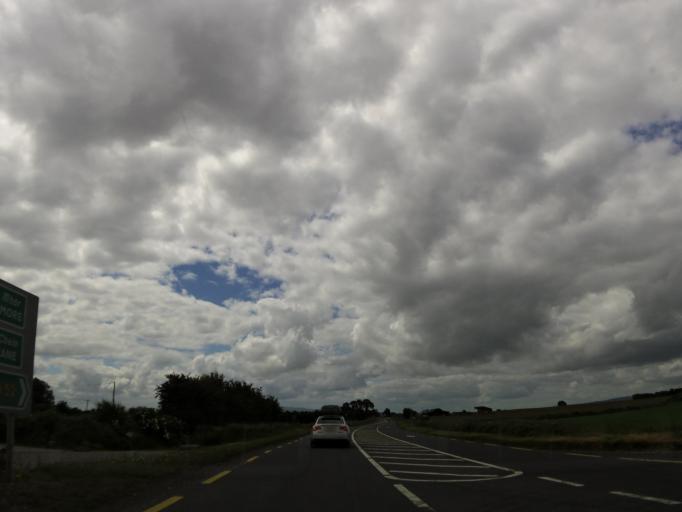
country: IE
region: Munster
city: Nenagh Bridge
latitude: 52.9159
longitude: -8.1754
